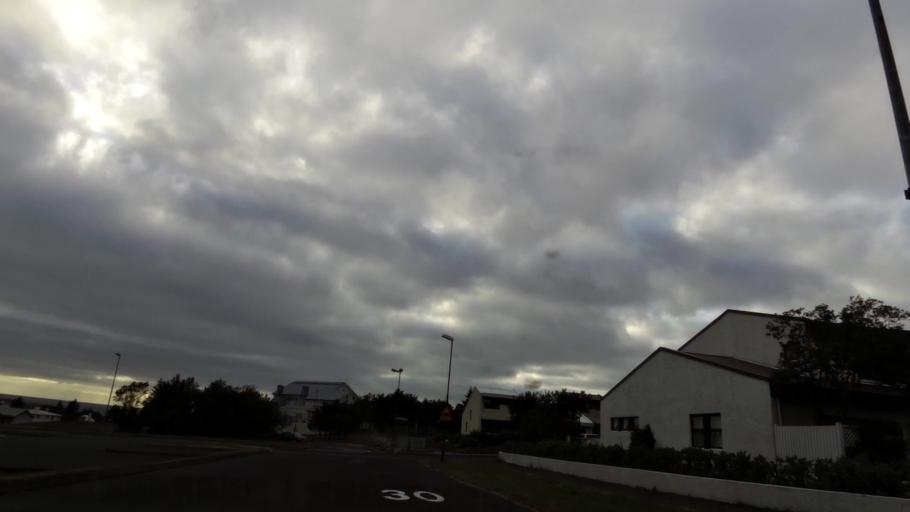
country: IS
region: Capital Region
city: Hafnarfjoerdur
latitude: 64.0603
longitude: -21.9529
